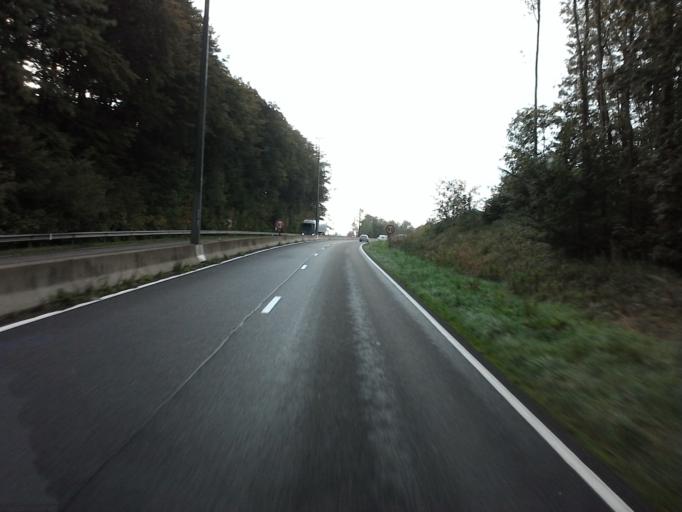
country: BE
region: Wallonia
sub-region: Province du Luxembourg
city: Attert
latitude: 49.7330
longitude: 5.7915
